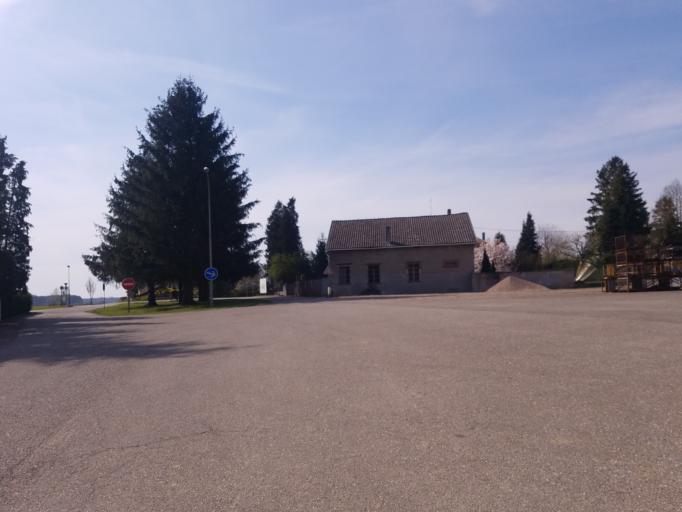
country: FR
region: Alsace
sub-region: Departement du Bas-Rhin
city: Soufflenheim
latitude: 48.8977
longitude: 7.9807
